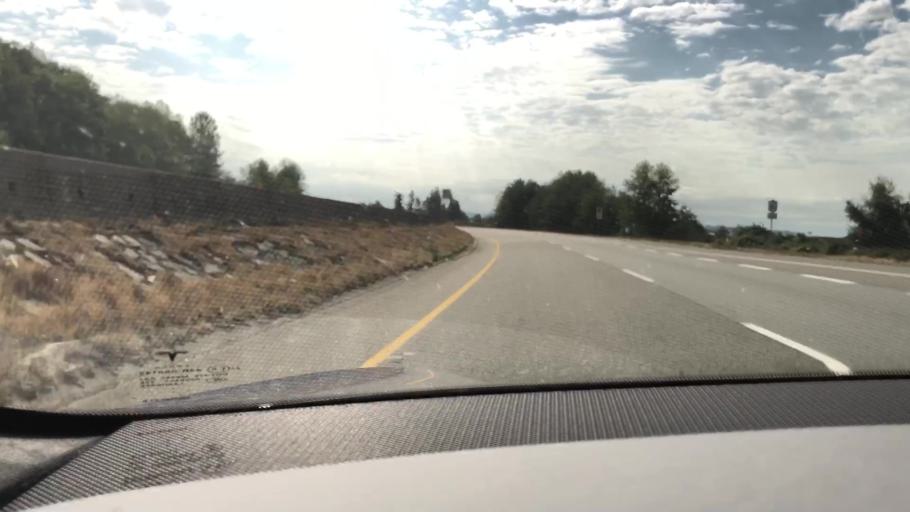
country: CA
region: British Columbia
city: Delta
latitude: 49.1177
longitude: -122.9256
